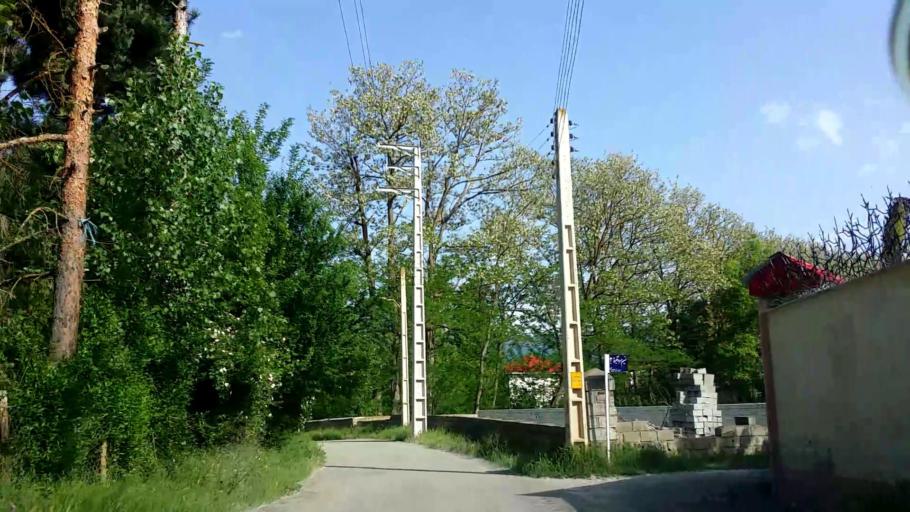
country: IR
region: Mazandaran
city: `Abbasabad
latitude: 36.5230
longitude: 51.1747
